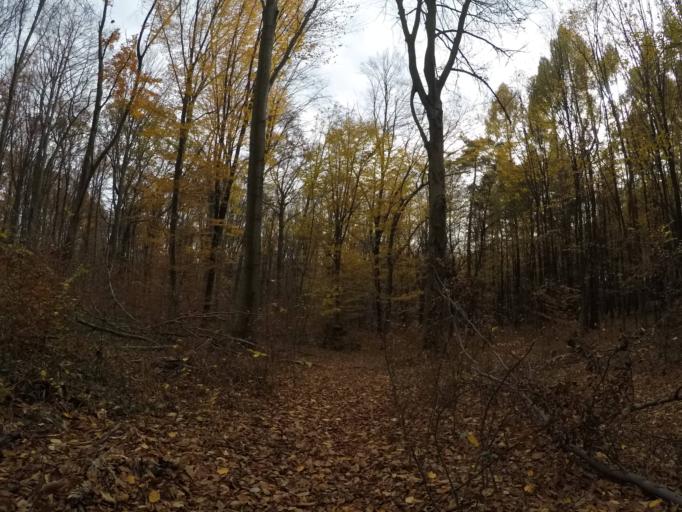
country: SK
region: Presovsky
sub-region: Okres Presov
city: Presov
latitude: 48.9610
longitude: 21.1822
